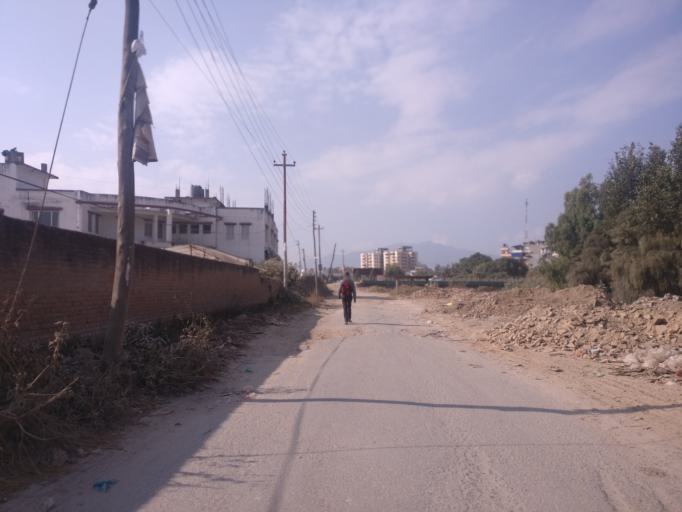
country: NP
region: Central Region
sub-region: Bagmati Zone
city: Patan
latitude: 27.6766
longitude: 85.3364
